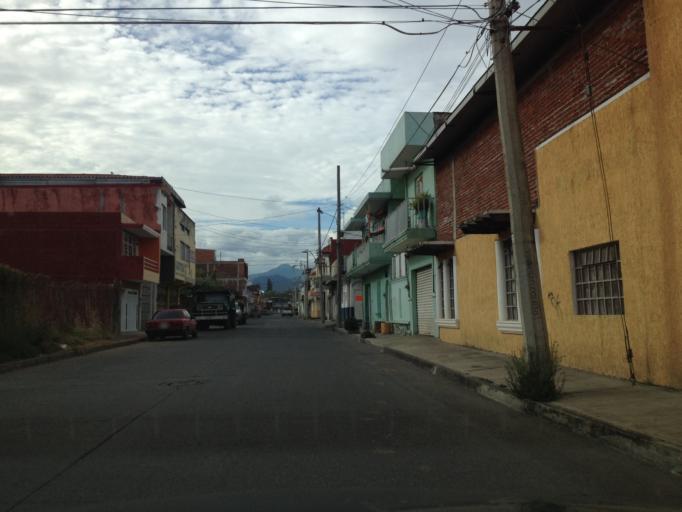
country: MX
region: Michoacan
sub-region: Uruapan
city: Uruapan
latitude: 19.4076
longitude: -102.0402
